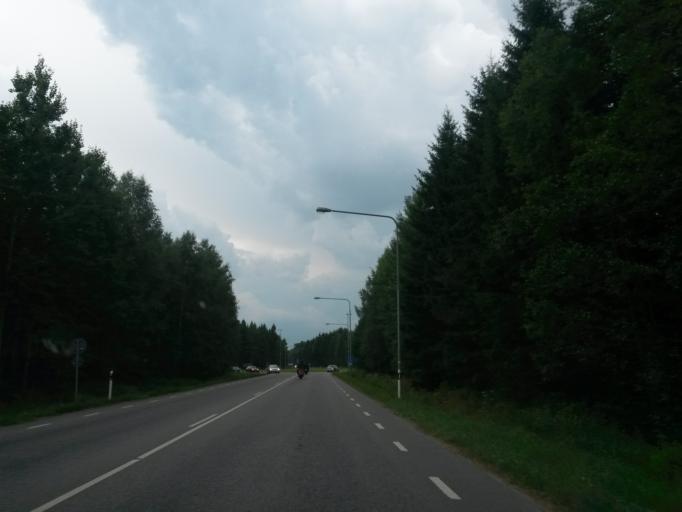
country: SE
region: Vaestra Goetaland
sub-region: Lidkopings Kommun
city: Lidkoping
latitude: 58.5203
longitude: 13.1134
